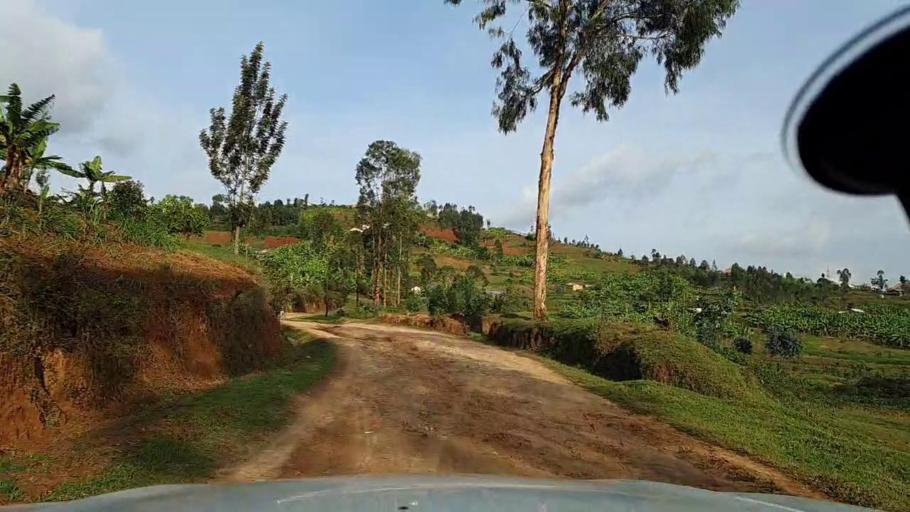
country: RW
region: Southern Province
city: Gitarama
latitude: -2.1820
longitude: 29.5606
